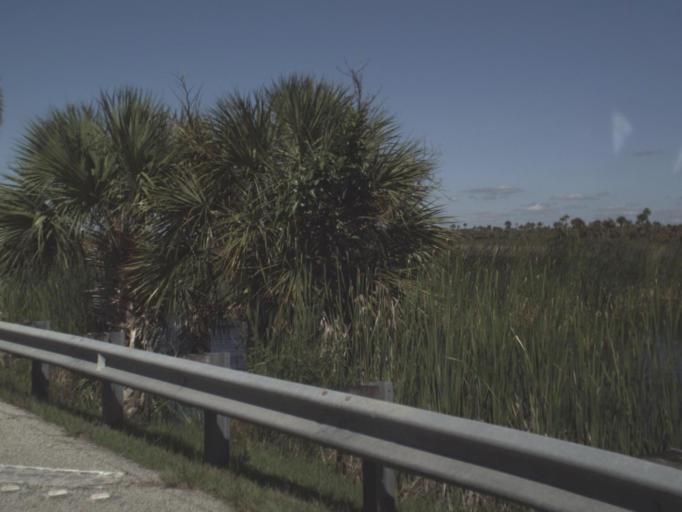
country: US
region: Florida
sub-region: Collier County
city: Marco
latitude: 25.9280
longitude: -81.4315
